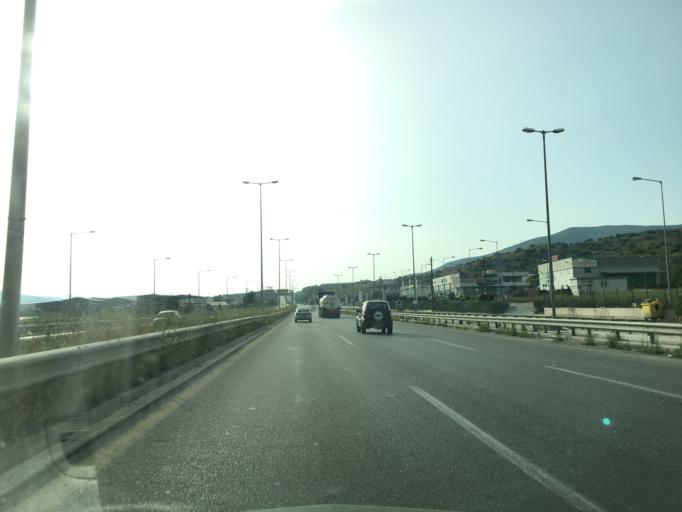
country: GR
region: Thessaly
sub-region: Nomos Magnisias
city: Nea Ionia
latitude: 39.3747
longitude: 22.9005
